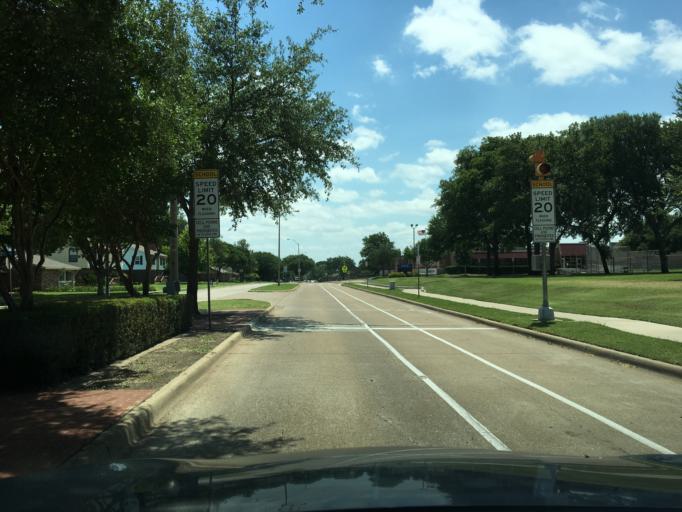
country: US
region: Texas
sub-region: Dallas County
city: Richardson
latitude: 32.9678
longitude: -96.6917
